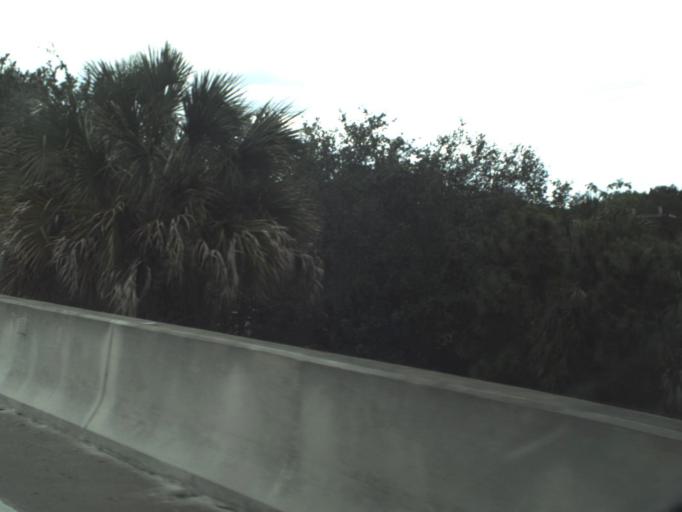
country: US
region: Florida
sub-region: Brevard County
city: Cocoa
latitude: 28.4013
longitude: -80.7467
